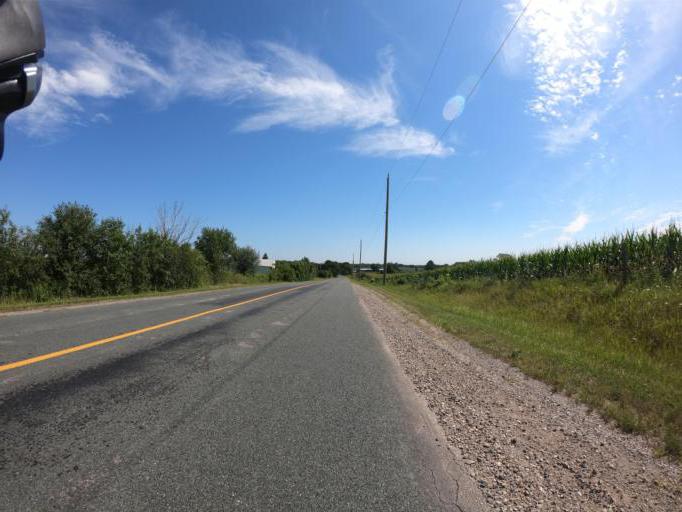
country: CA
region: Ontario
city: Waterloo
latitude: 43.4980
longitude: -80.4253
